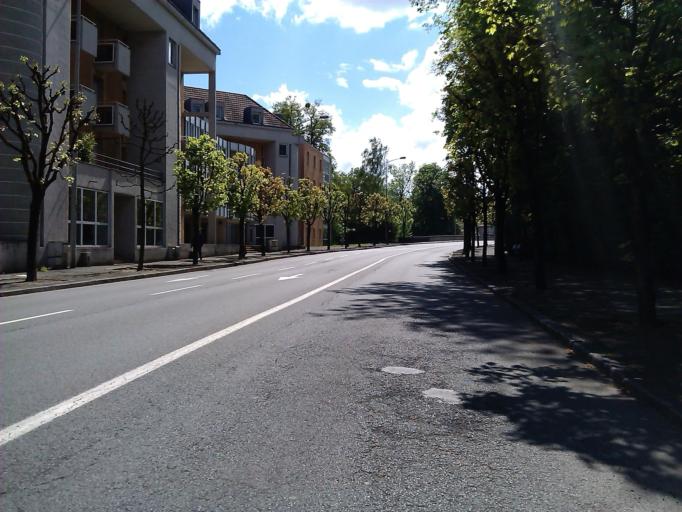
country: FR
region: Franche-Comte
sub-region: Departement du Doubs
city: Arbouans
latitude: 47.5067
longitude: 6.7975
